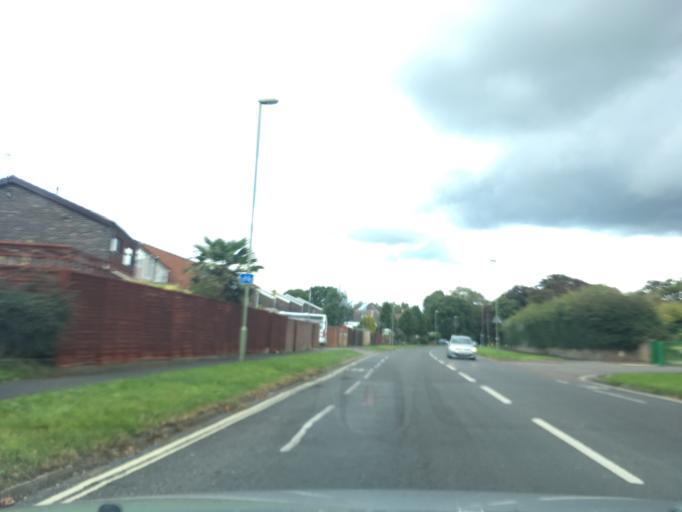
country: GB
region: England
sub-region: Hampshire
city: Havant
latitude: 50.8600
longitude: -0.9731
